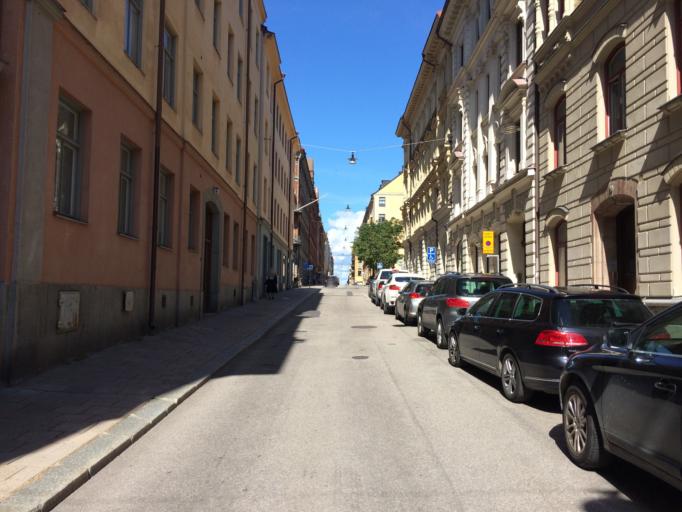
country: SE
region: Stockholm
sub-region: Stockholms Kommun
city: OEstermalm
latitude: 59.3328
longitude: 18.0820
